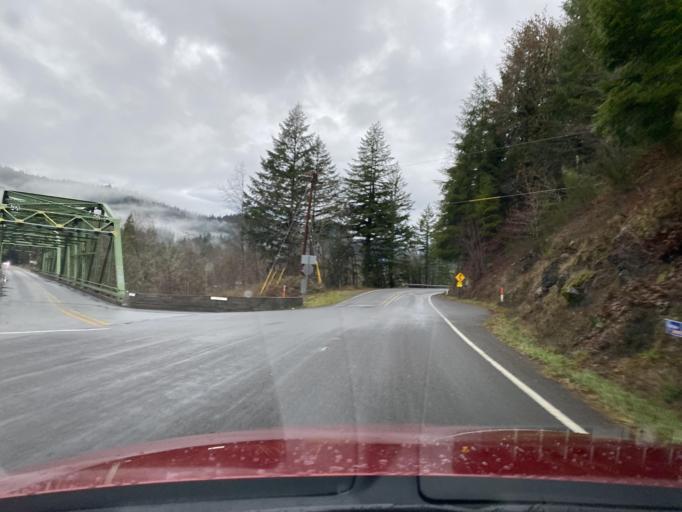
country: US
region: Oregon
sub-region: Lane County
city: Oakridge
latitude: 43.7542
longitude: -122.5259
